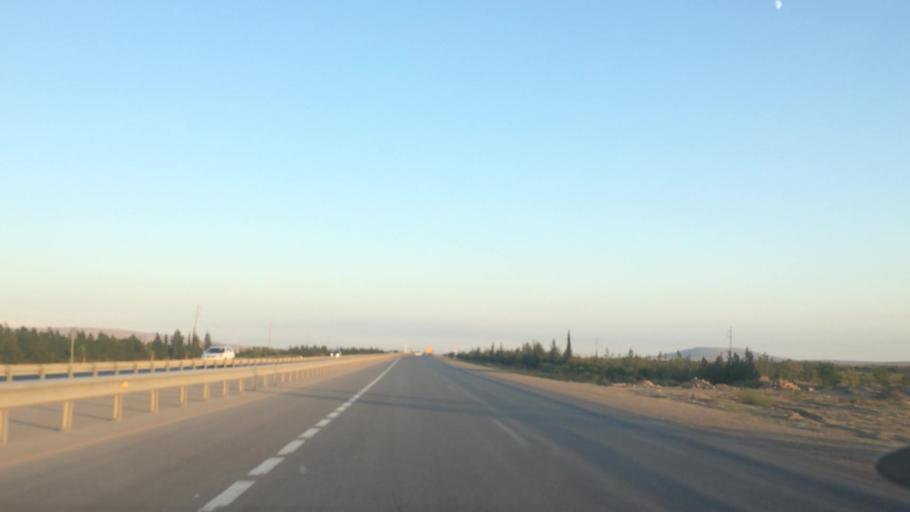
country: AZ
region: Haciqabul
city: Haciqabul
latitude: 40.0054
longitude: 49.1616
